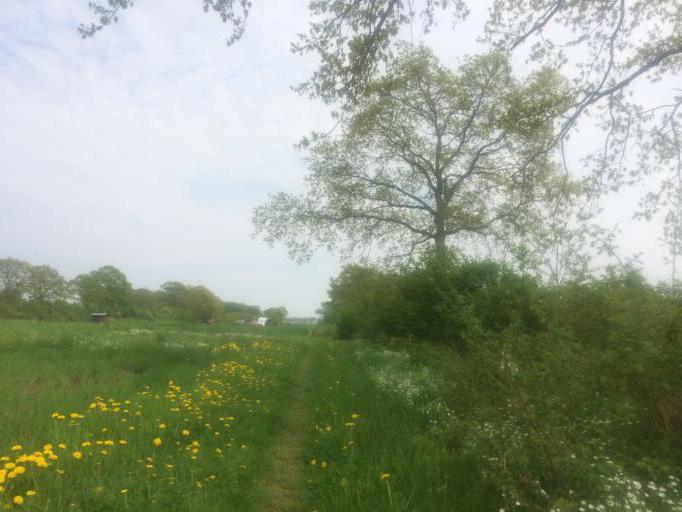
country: SE
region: Kalmar
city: Faerjestaden
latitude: 56.6074
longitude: 16.4393
